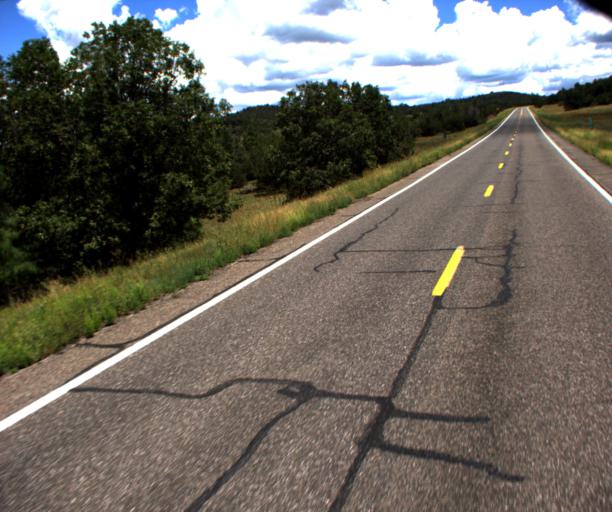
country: US
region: Arizona
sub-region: Gila County
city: Pine
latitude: 34.5075
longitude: -111.5642
